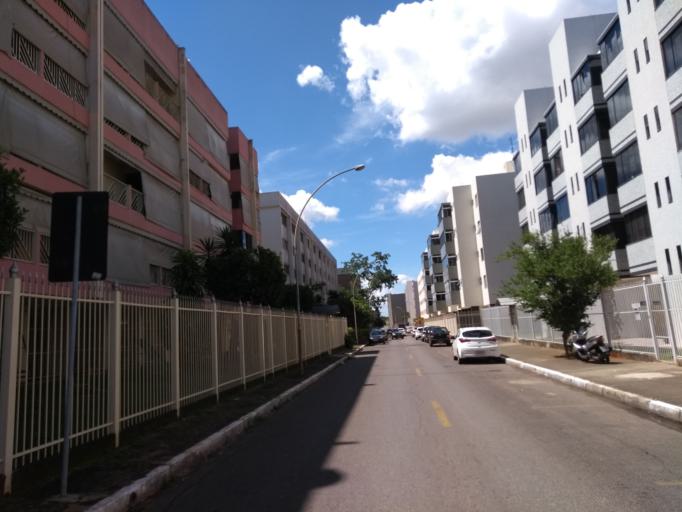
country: BR
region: Federal District
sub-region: Brasilia
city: Brasilia
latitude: -15.7936
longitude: -47.9342
